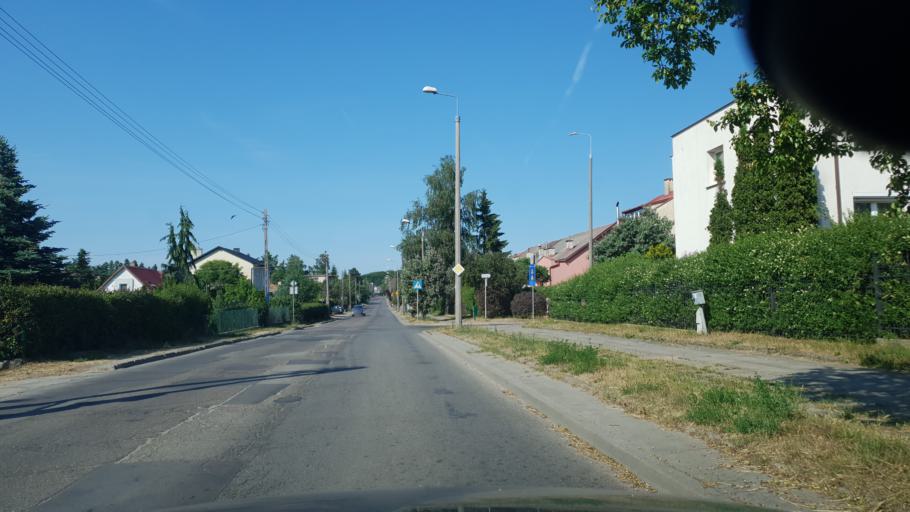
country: PL
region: Pomeranian Voivodeship
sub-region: Gdynia
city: Wielki Kack
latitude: 54.4305
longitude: 18.4624
